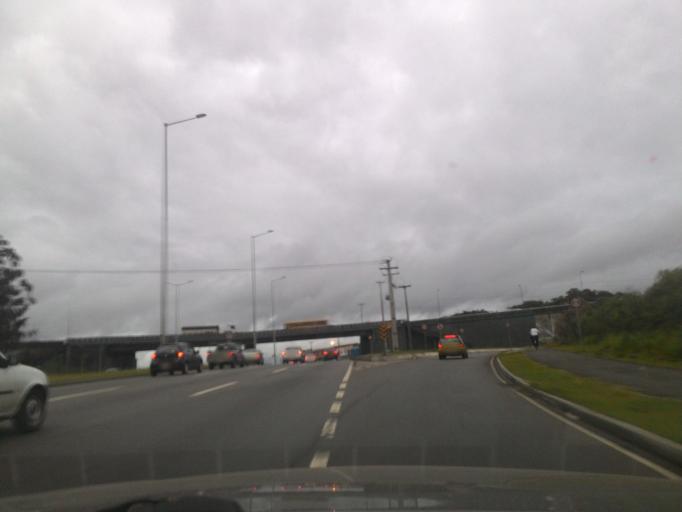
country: BR
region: Parana
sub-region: Pinhais
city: Pinhais
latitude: -25.4450
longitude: -49.2342
